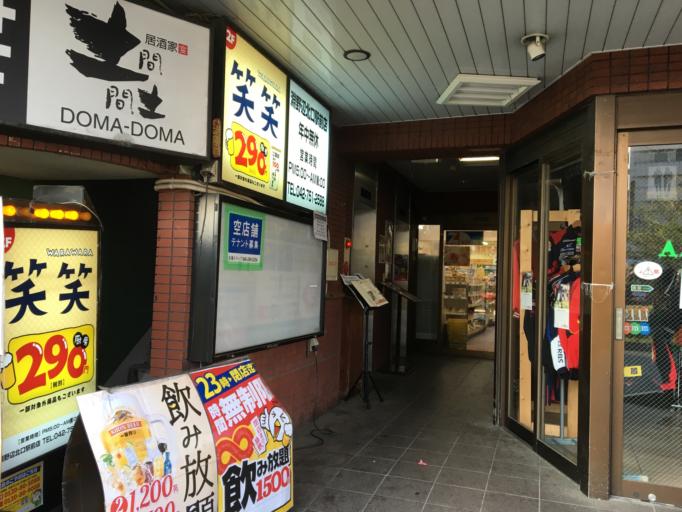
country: JP
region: Tokyo
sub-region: Machida-shi
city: Machida
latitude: 35.5696
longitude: 139.3942
